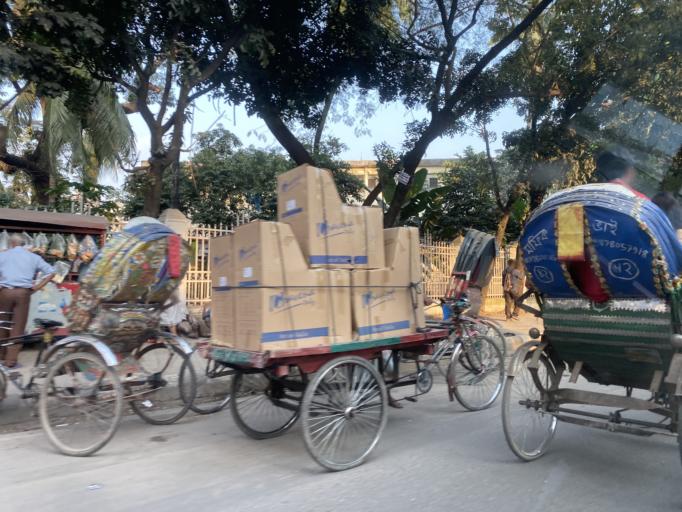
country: BD
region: Dhaka
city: Azimpur
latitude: 23.7288
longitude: 90.3964
